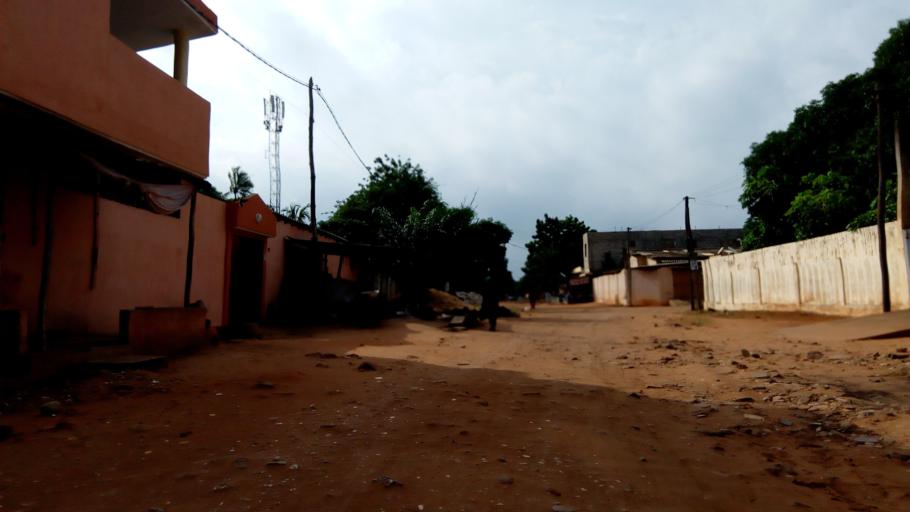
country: TG
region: Maritime
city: Lome
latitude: 6.1817
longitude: 1.1929
